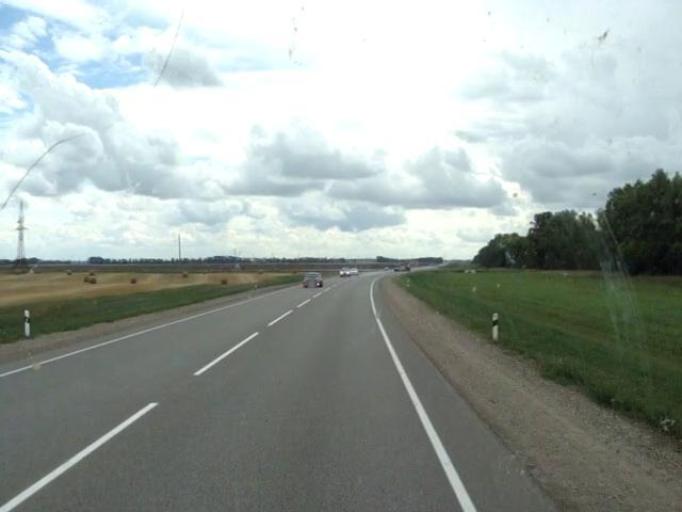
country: RU
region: Altai Krai
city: Shubenka
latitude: 52.6789
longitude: 85.0495
